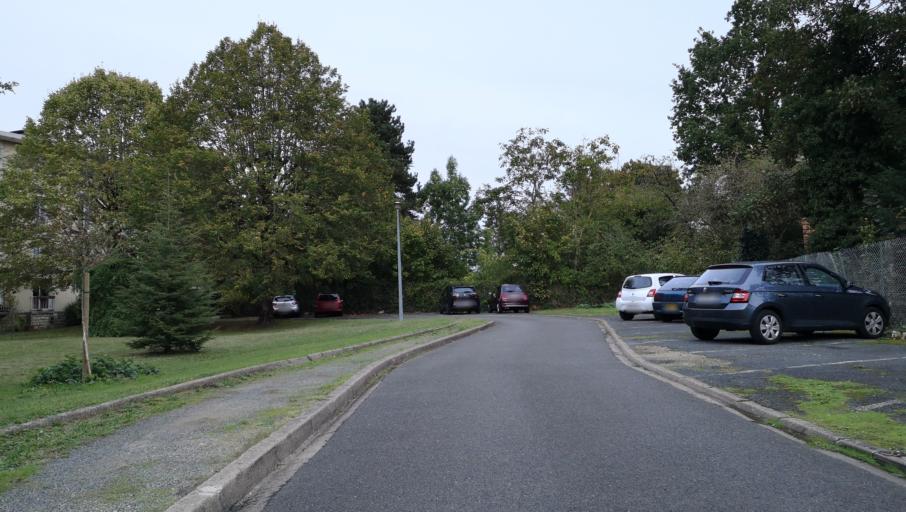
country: FR
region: Centre
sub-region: Departement du Loiret
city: Saint-Jean-le-Blanc
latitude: 47.9041
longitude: 1.9243
